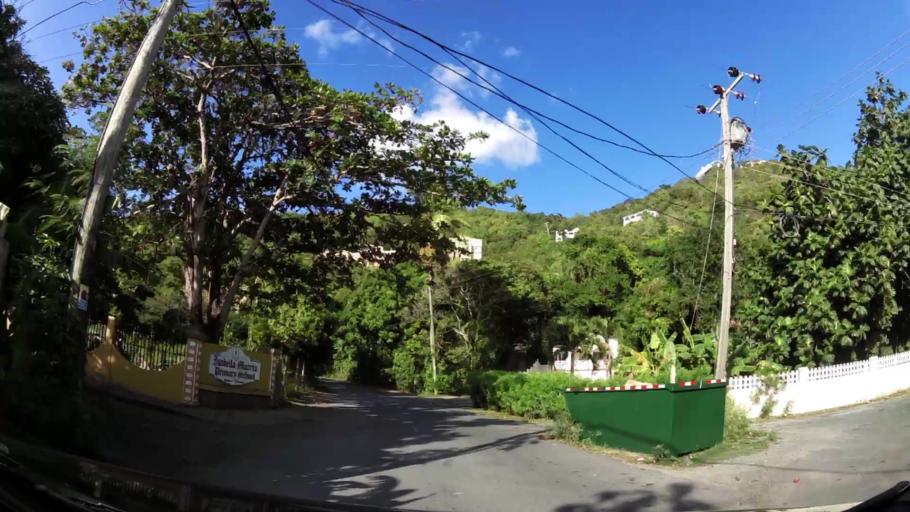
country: VG
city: Road Town
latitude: 18.4140
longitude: -64.6702
